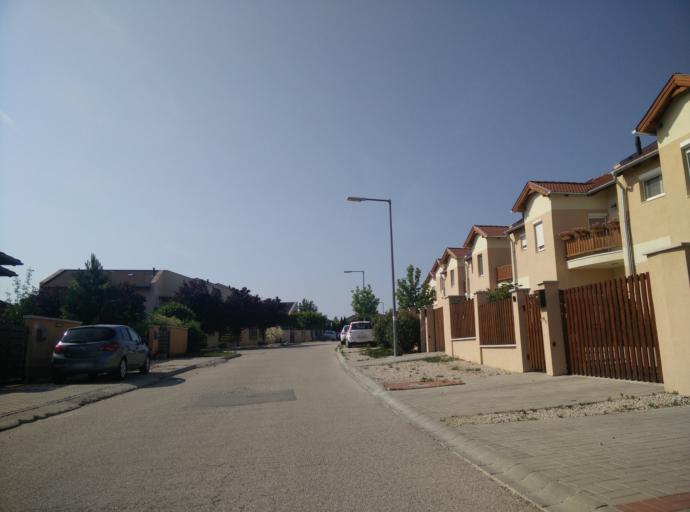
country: HU
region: Pest
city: Biatorbagy
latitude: 47.4781
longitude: 18.8155
